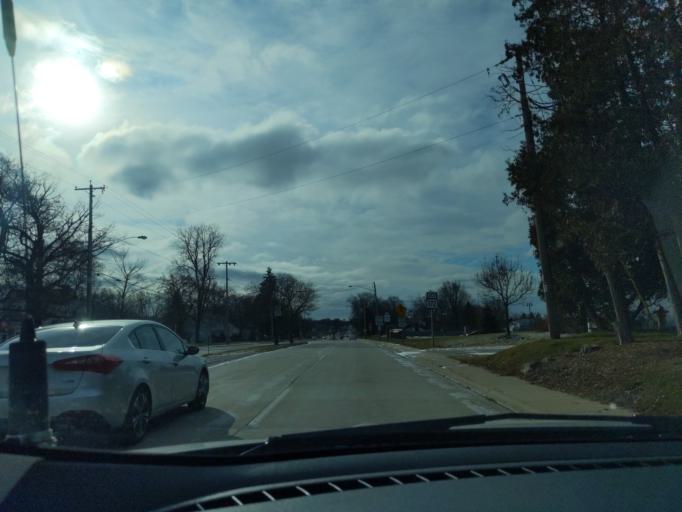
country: US
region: Wisconsin
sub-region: Brown County
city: Allouez
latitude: 44.4743
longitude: -88.0290
